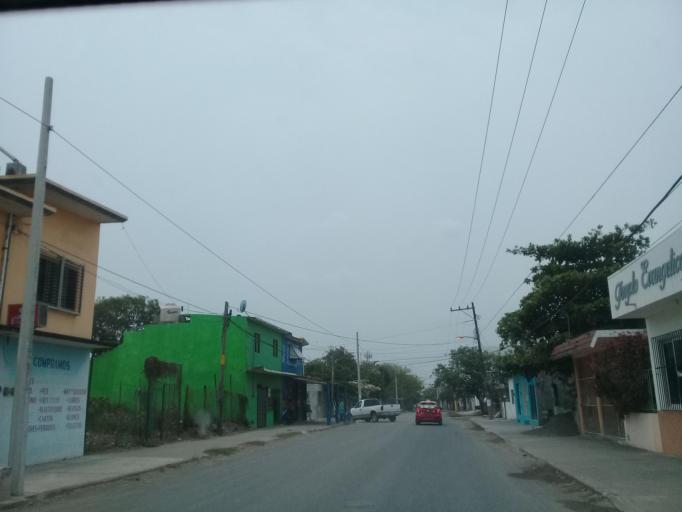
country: MX
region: Veracruz
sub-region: Veracruz
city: Las Amapolas
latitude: 19.1443
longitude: -96.2014
